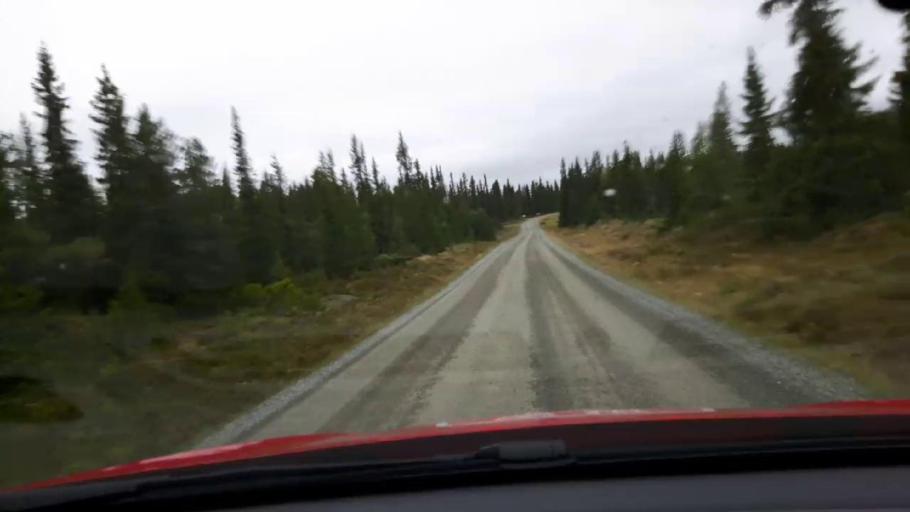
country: SE
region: Jaemtland
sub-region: Bergs Kommun
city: Hoverberg
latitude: 62.8731
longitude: 13.9665
